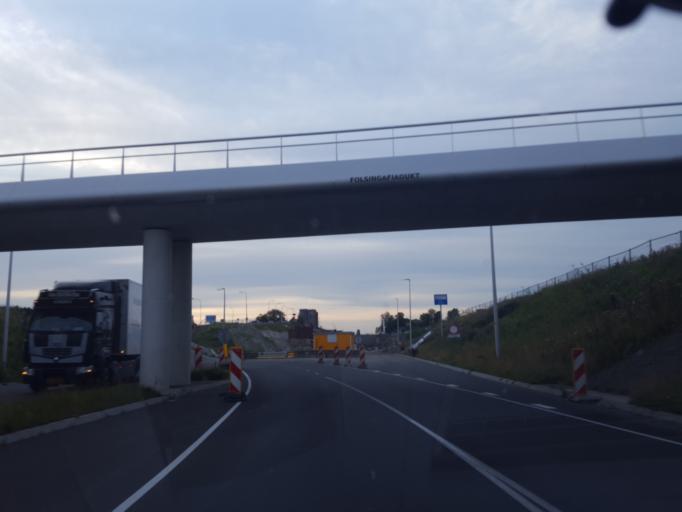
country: NL
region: Friesland
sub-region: Gemeente Leeuwarden
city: Huizum
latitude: 53.1816
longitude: 5.8207
